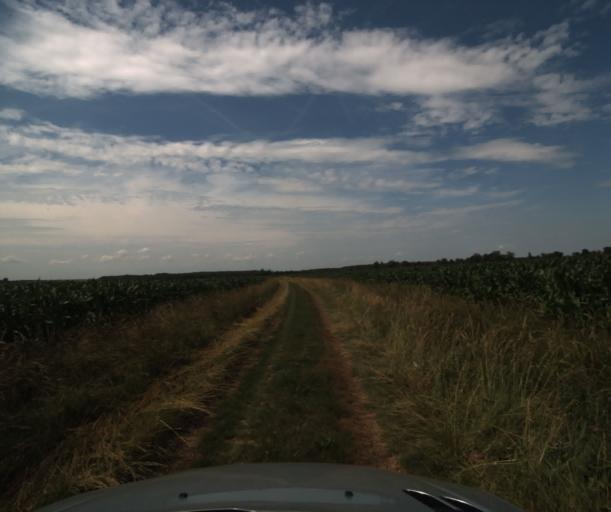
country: FR
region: Midi-Pyrenees
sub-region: Departement de la Haute-Garonne
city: Labastidette
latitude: 43.4789
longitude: 1.2230
